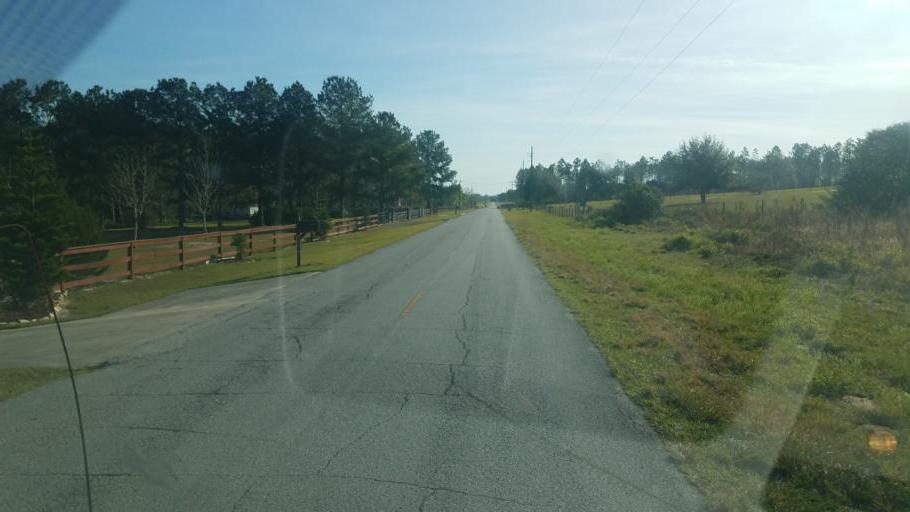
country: US
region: Florida
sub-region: Lake County
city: Clermont
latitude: 28.4615
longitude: -81.7762
